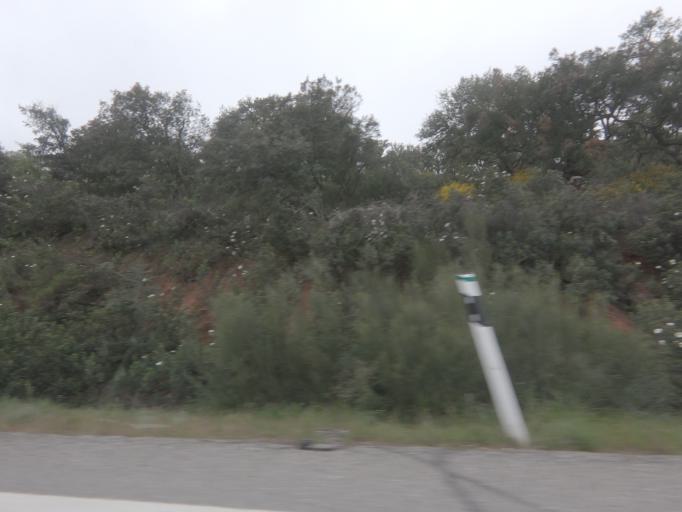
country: ES
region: Extremadura
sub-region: Provincia de Badajoz
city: Puebla de Obando
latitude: 39.2748
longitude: -6.5207
